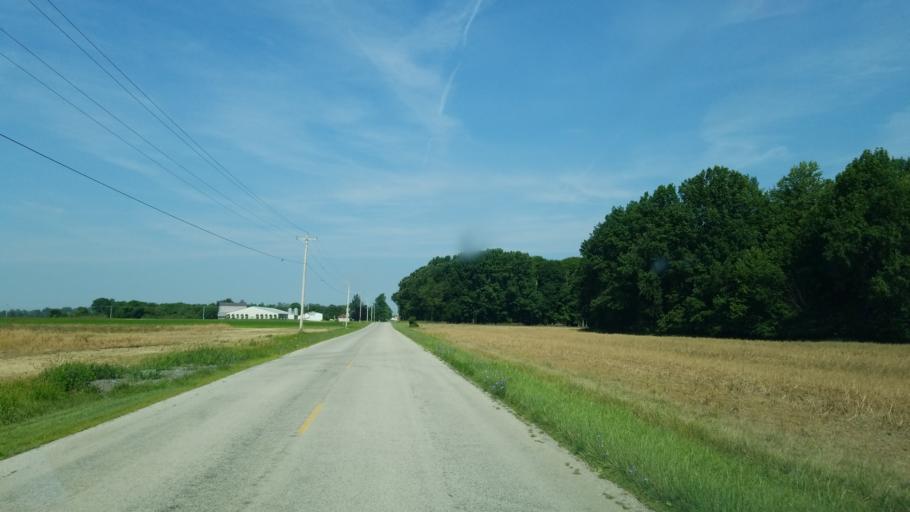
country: US
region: Ohio
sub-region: Sandusky County
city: Mount Carmel
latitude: 41.0586
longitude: -82.9514
